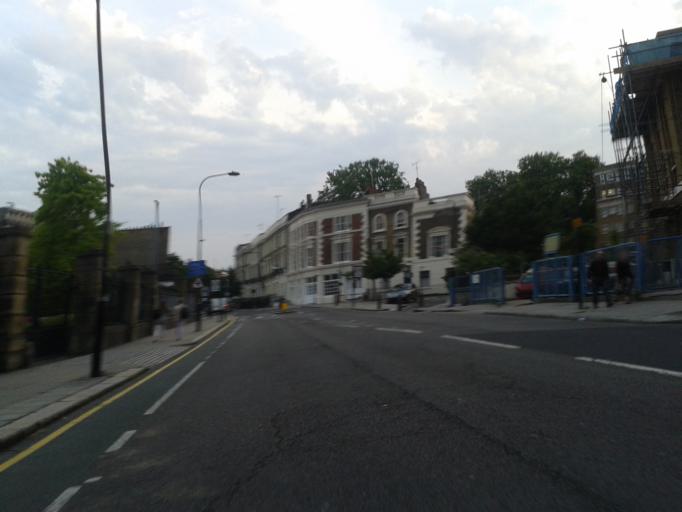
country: GB
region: England
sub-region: Greater London
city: Clerkenwell
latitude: 51.5261
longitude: -0.1135
